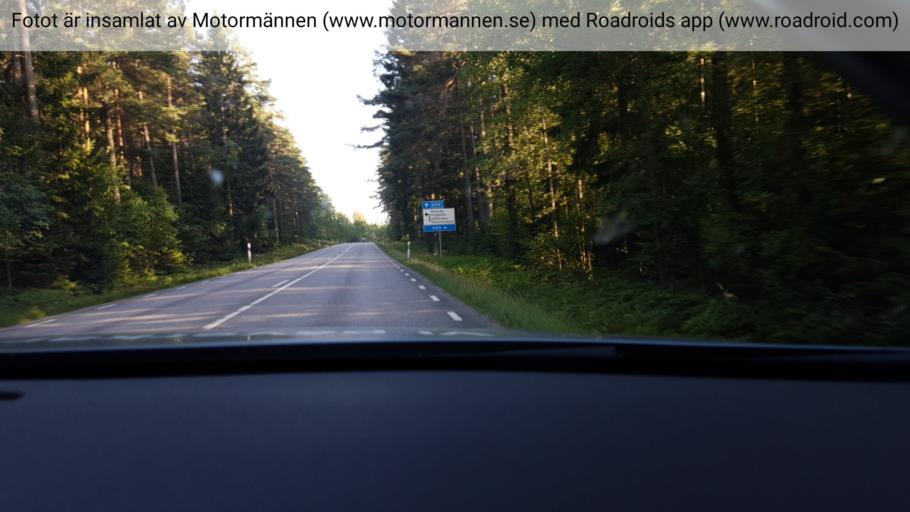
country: SE
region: Vaestra Goetaland
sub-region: Skovde Kommun
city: Stopen
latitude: 58.4541
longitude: 13.9548
